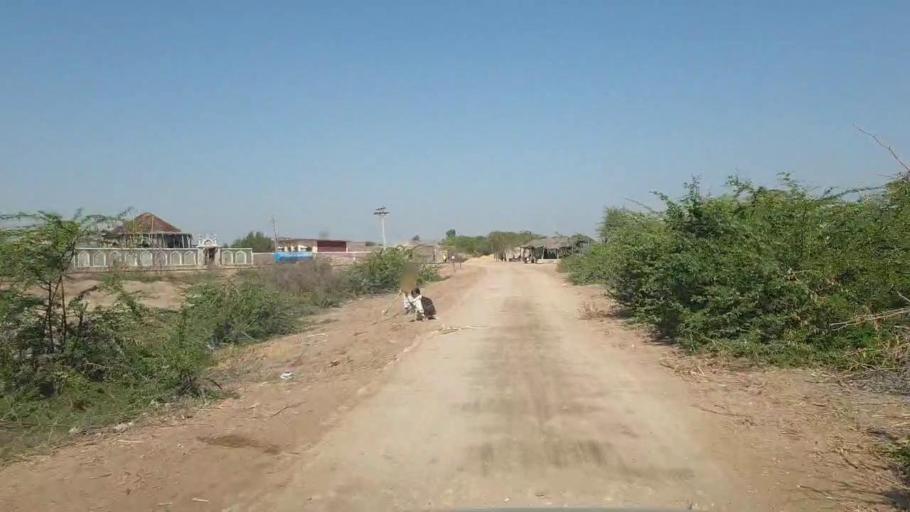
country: PK
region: Sindh
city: Digri
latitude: 25.2537
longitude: 69.2282
